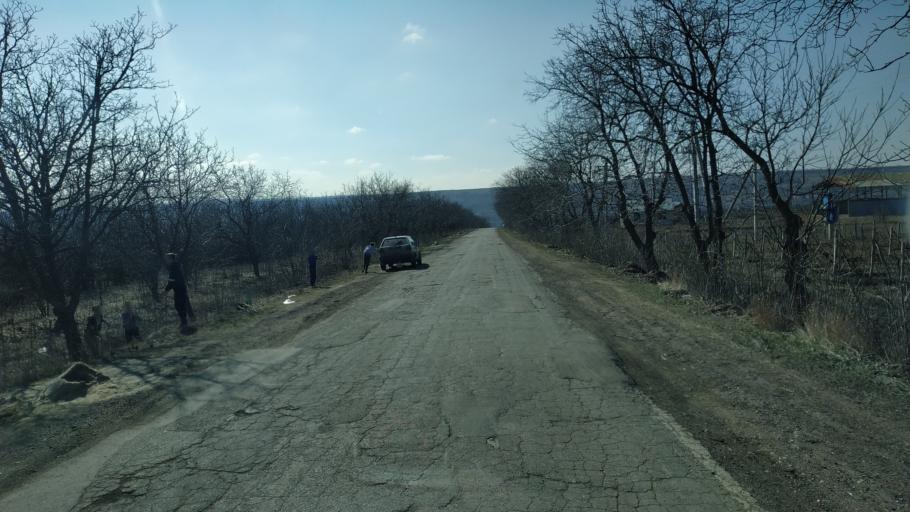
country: MD
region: Hincesti
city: Hincesti
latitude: 46.7605
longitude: 28.6653
